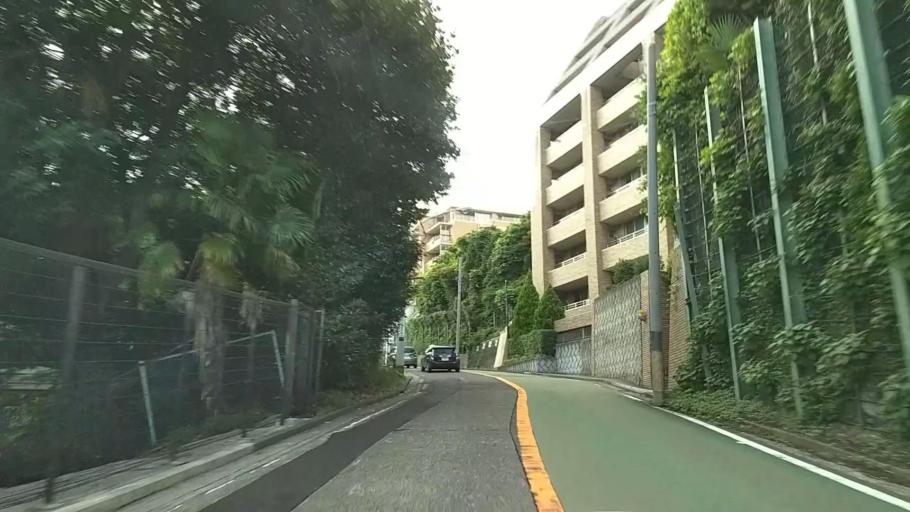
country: JP
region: Kanagawa
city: Yokohama
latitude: 35.4192
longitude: 139.6386
